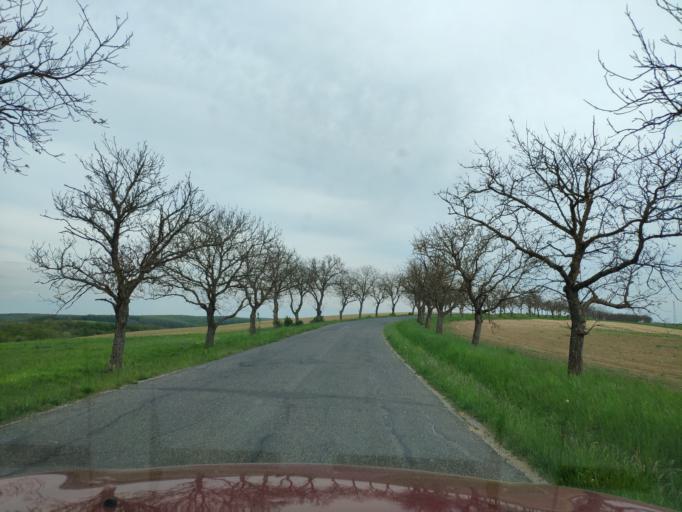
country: SK
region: Banskobystricky
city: Revuca
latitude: 48.4969
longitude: 20.2407
